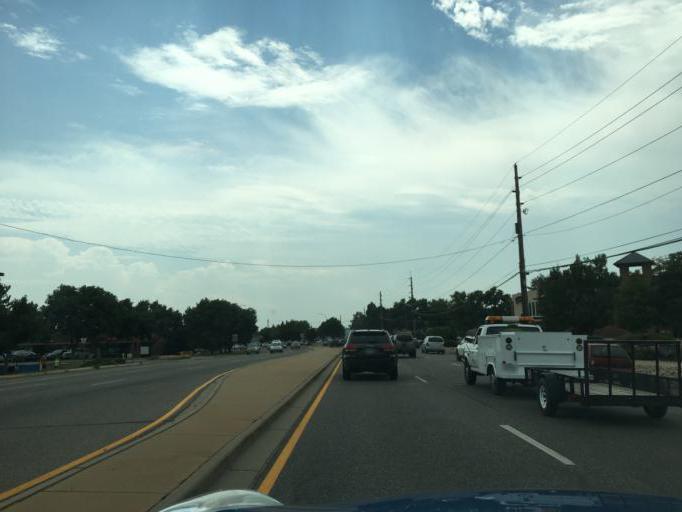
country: US
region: Colorado
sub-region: Jefferson County
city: Arvada
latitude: 39.8162
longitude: -105.0815
